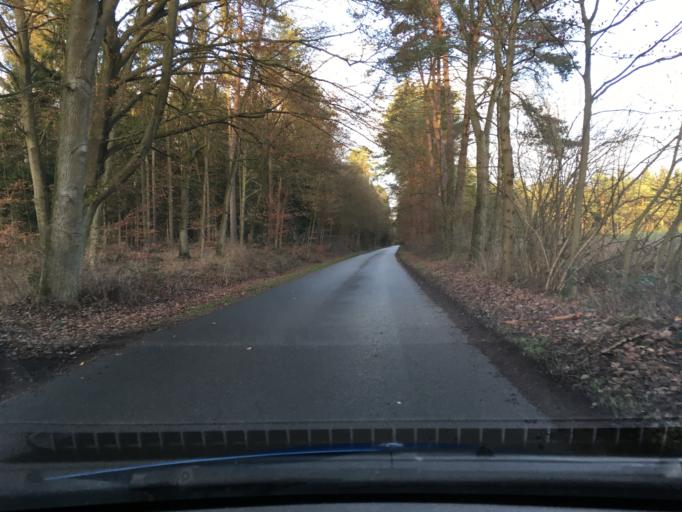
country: DE
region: Lower Saxony
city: Soderstorf
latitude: 53.0946
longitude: 10.1521
